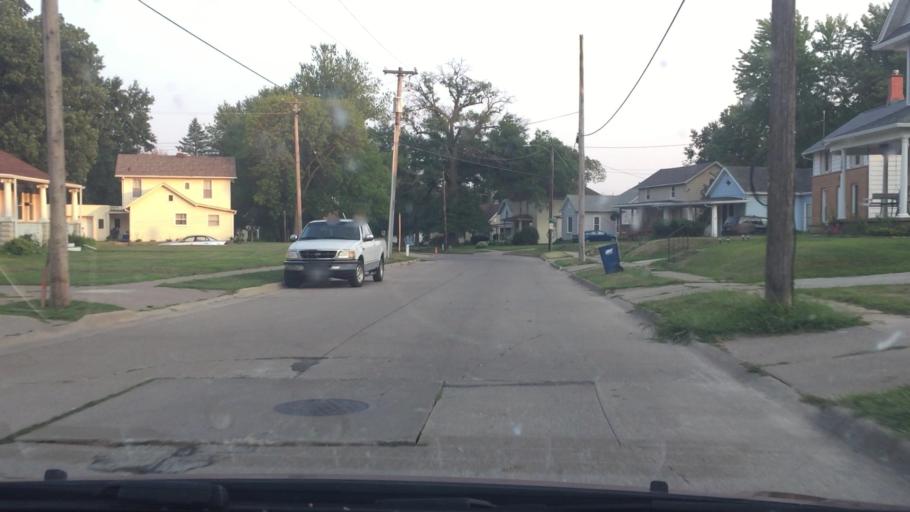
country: US
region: Iowa
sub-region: Muscatine County
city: Muscatine
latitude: 41.4337
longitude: -91.0478
